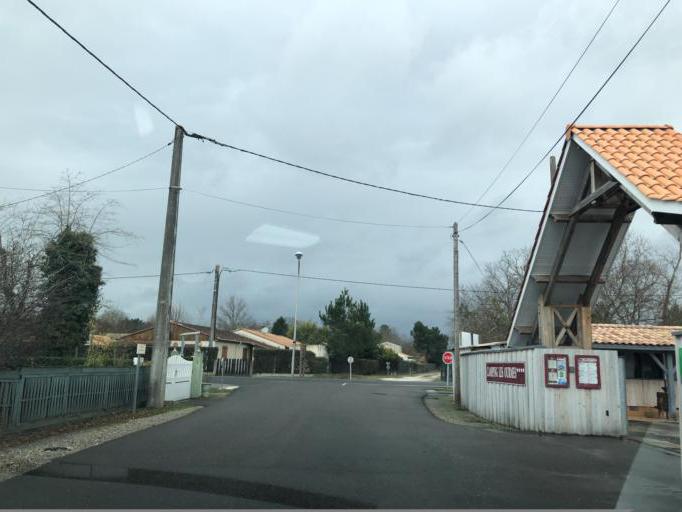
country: FR
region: Aquitaine
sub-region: Departement de la Gironde
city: Hourtin
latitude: 45.1818
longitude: -1.0758
